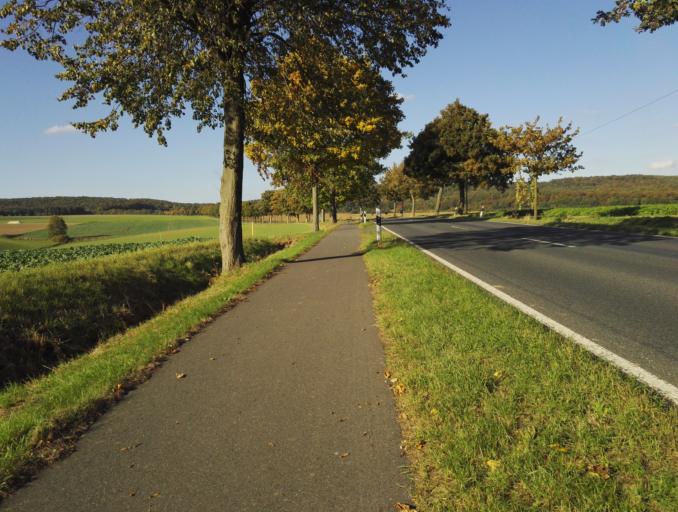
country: DE
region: Lower Saxony
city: Holle
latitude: 52.1111
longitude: 10.1071
